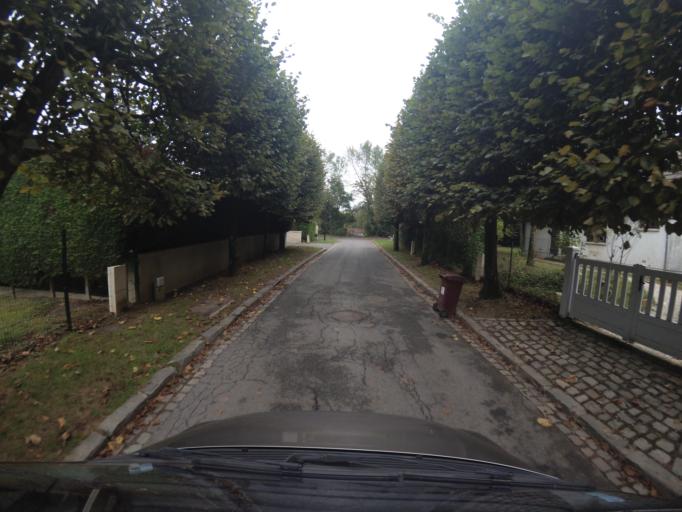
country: FR
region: Ile-de-France
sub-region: Departement de Seine-et-Marne
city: Collegien
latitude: 48.8426
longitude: 2.6734
